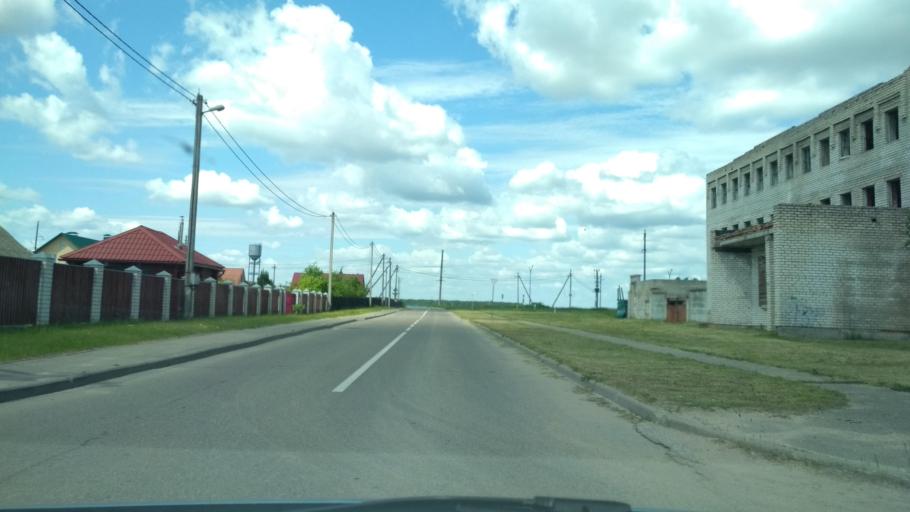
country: BY
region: Grodnenskaya
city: Astravyets
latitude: 54.6220
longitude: 25.9582
